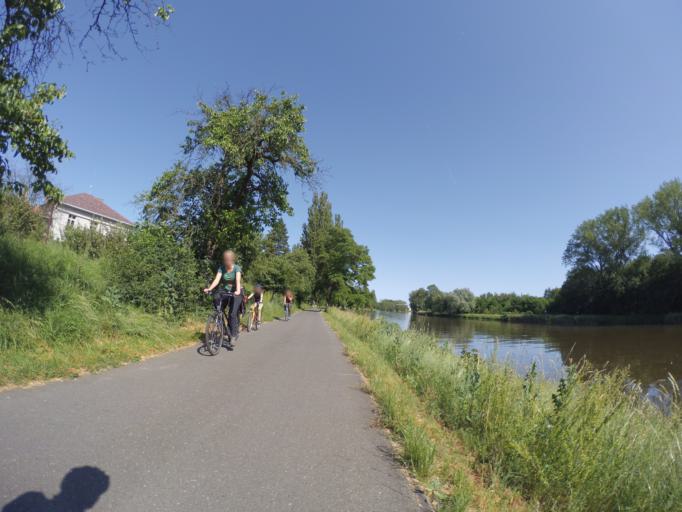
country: CZ
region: Central Bohemia
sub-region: Okres Nymburk
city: Podebrady
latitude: 50.1609
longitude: 15.0979
